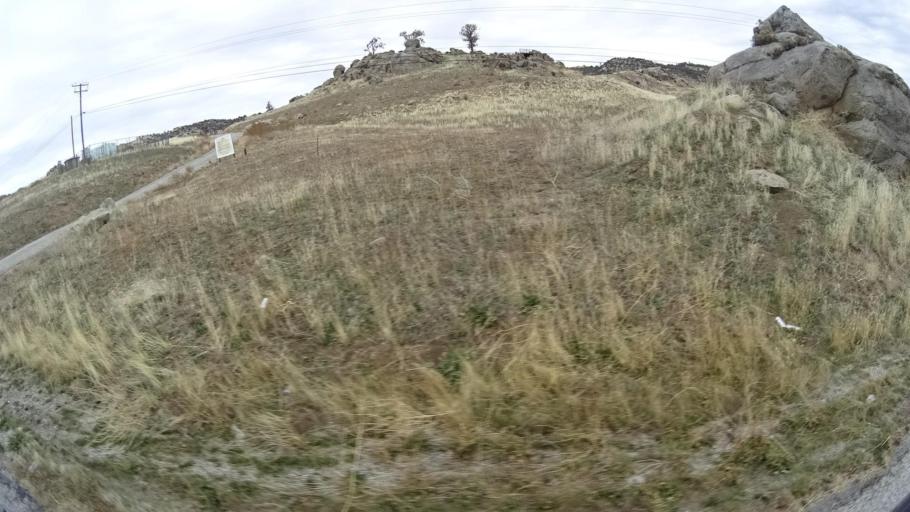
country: US
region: California
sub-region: Kern County
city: Bear Valley Springs
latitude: 35.1233
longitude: -118.6138
